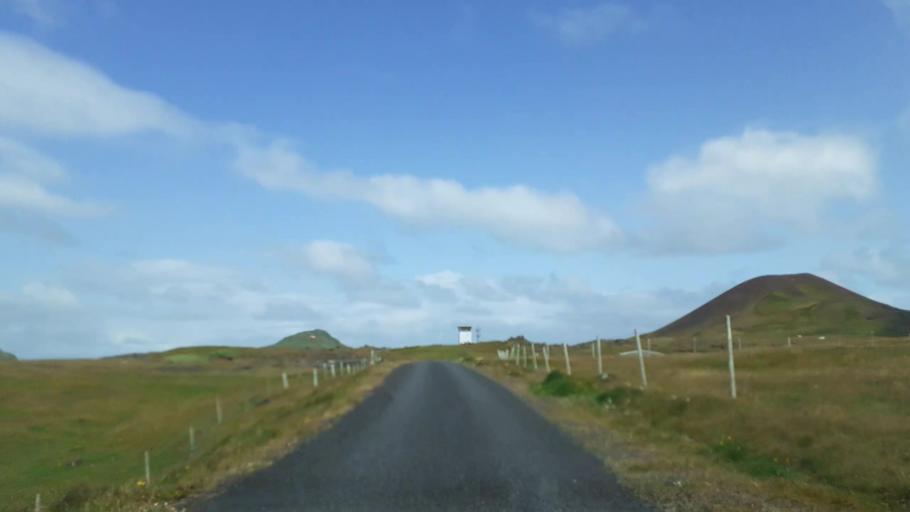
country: IS
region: South
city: Vestmannaeyjar
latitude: 63.4226
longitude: -20.2774
